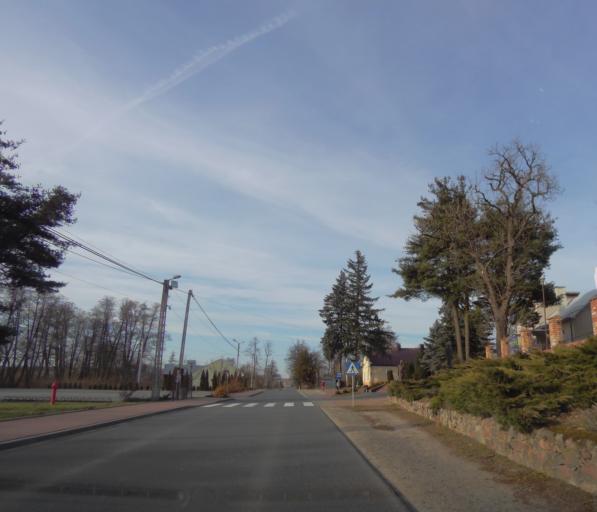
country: PL
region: Subcarpathian Voivodeship
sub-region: Powiat lezajski
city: Giedlarowa
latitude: 50.2354
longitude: 22.4196
